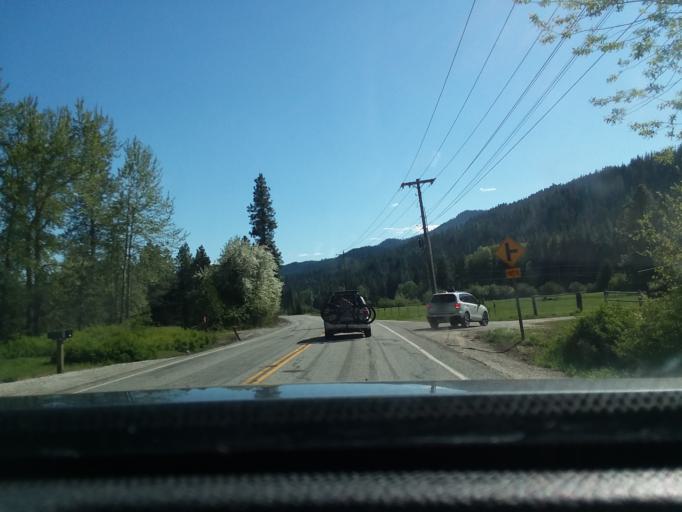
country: US
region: Washington
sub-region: Chelan County
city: Leavenworth
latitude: 47.7826
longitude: -120.6673
